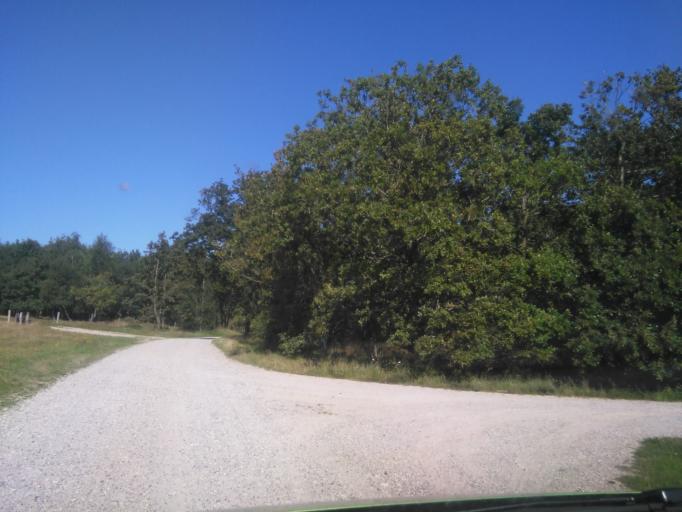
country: DK
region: Central Jutland
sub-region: Syddjurs Kommune
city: Ronde
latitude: 56.2079
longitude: 10.5331
